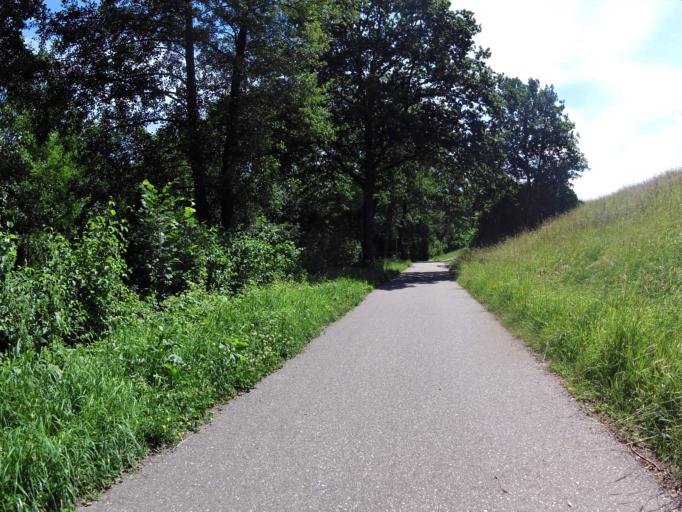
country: DE
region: Baden-Wuerttemberg
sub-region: Freiburg Region
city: Hohberg
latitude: 48.3358
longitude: 7.9103
